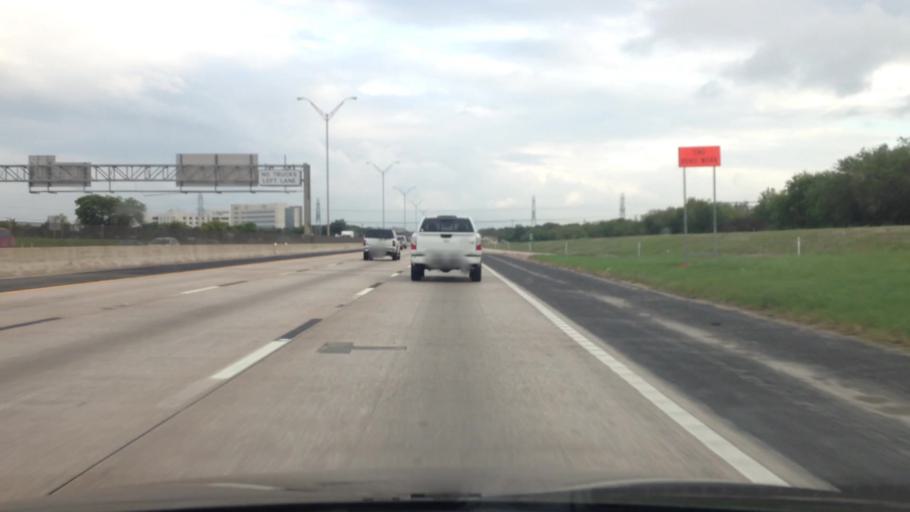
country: US
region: Texas
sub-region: Tarrant County
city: Crowley
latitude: 32.5952
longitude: -97.3196
